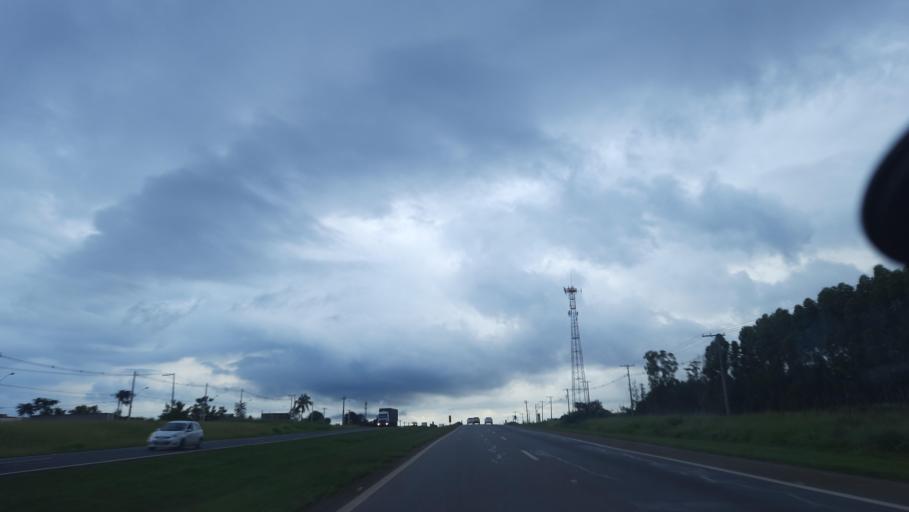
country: BR
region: Sao Paulo
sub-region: Moji-Guacu
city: Mogi-Gaucu
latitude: -22.3371
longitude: -46.9587
